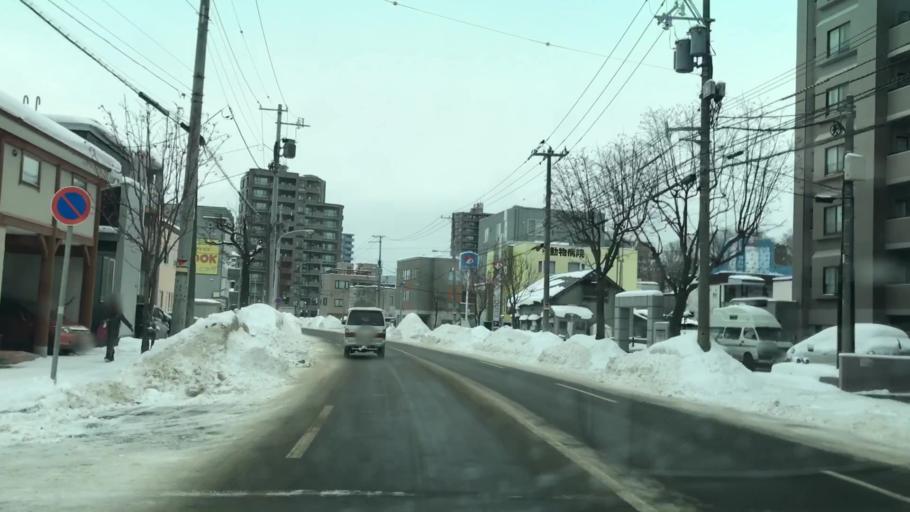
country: JP
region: Hokkaido
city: Sapporo
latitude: 43.0342
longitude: 141.3870
